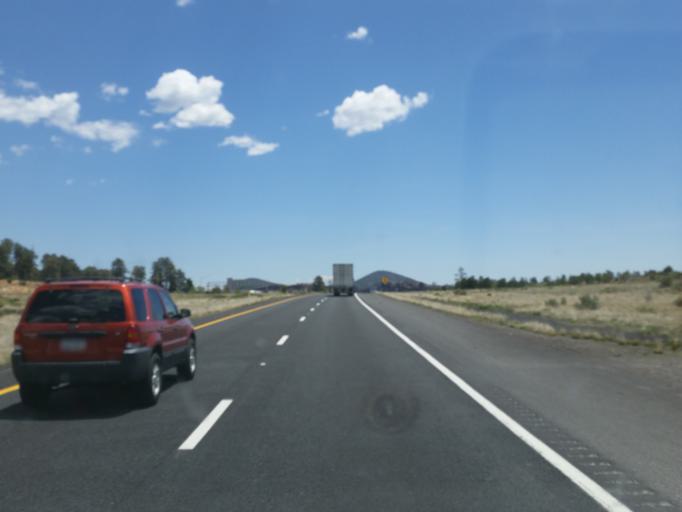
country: US
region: Arizona
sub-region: Coconino County
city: Flagstaff
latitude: 35.2165
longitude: -111.5815
